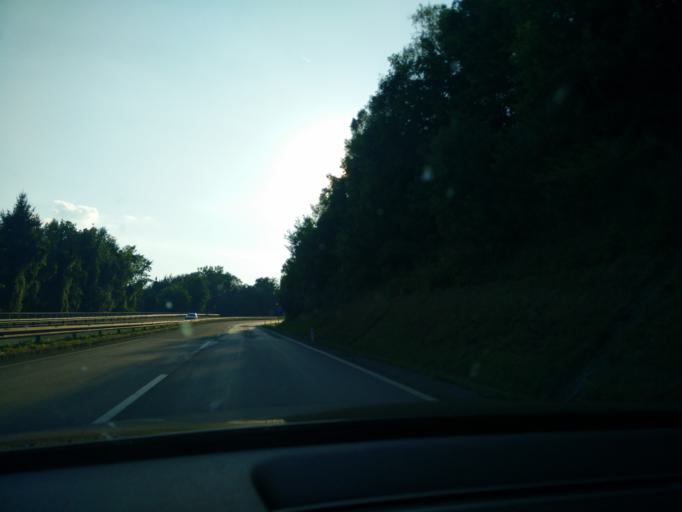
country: AT
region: Carinthia
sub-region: Politischer Bezirk Klagenfurt Land
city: Kottmannsdorf
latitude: 46.5446
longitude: 14.2555
